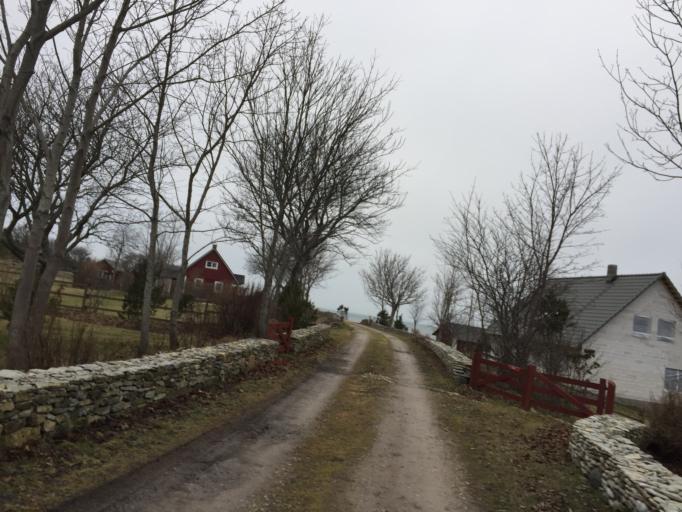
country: EE
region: Saare
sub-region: Kuressaare linn
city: Kuressaare
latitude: 58.5456
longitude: 22.2161
